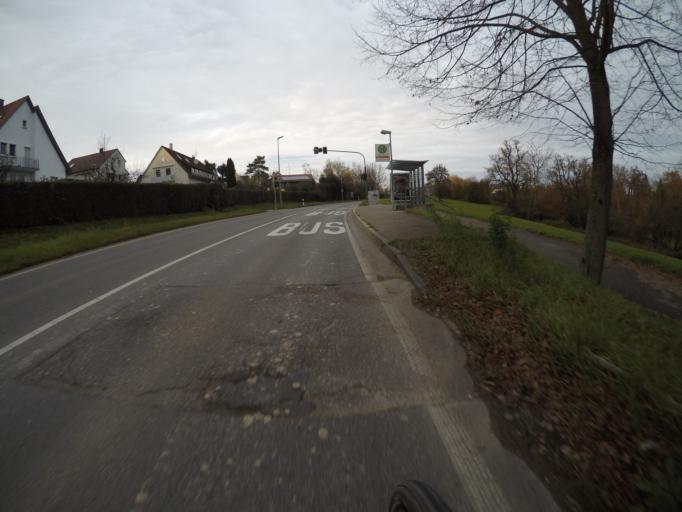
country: DE
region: Baden-Wuerttemberg
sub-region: Regierungsbezirk Stuttgart
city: Ostfildern
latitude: 48.7098
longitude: 9.2718
